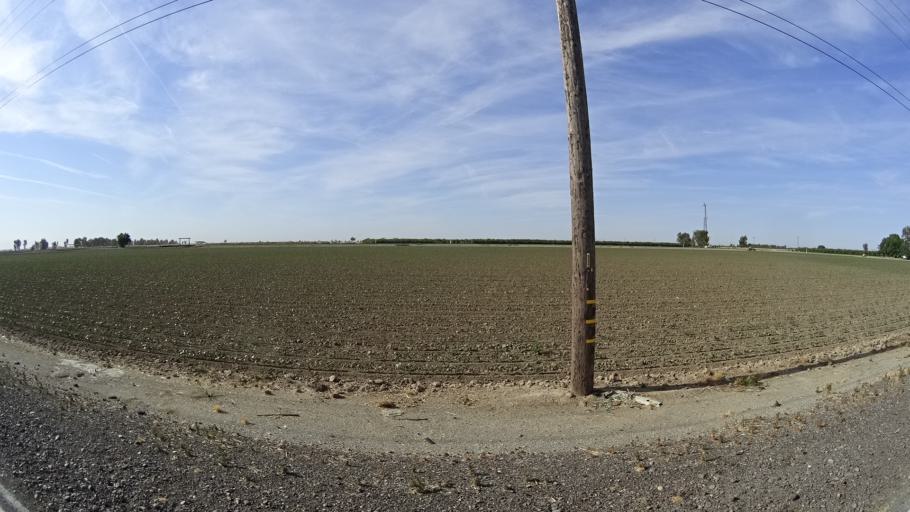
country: US
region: California
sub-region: Kings County
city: Home Garden
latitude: 36.3429
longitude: -119.5440
